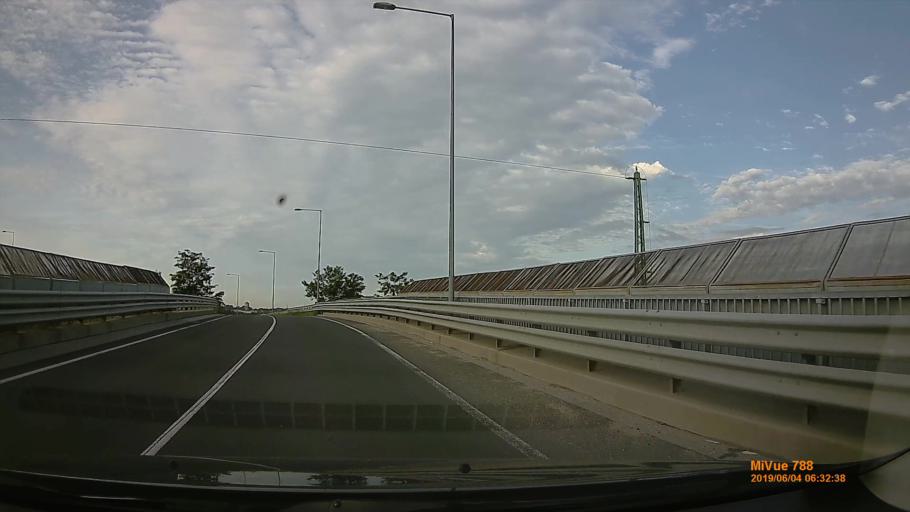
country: HU
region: Pest
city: Diosd
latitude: 47.3983
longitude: 18.9682
